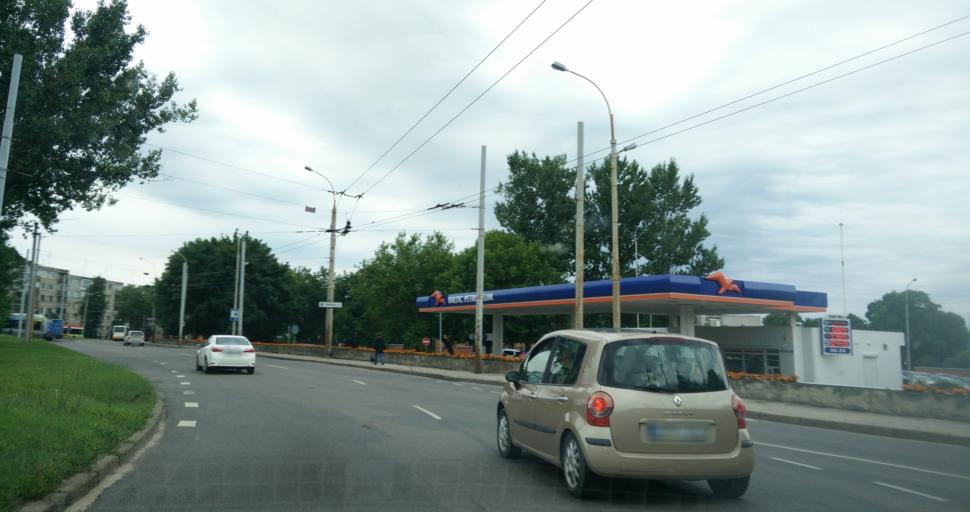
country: LT
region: Vilnius County
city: Rasos
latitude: 54.7226
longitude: 25.3176
